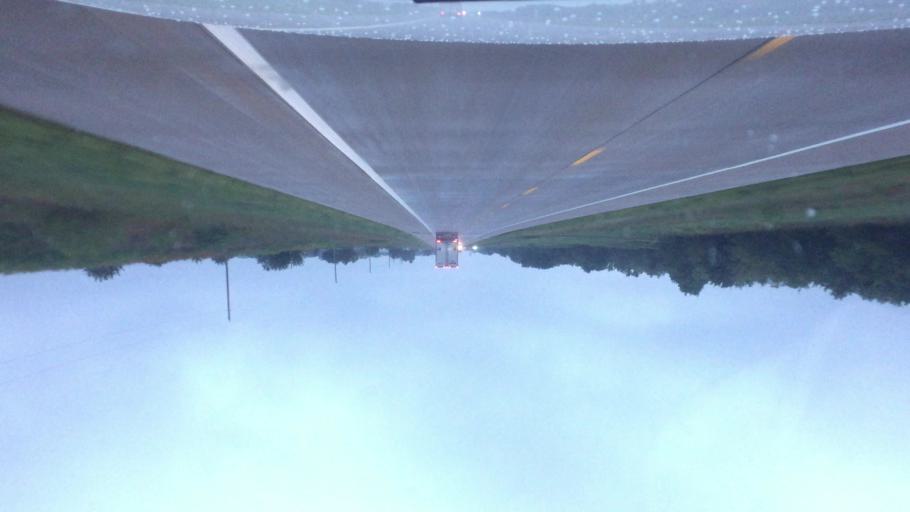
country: US
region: Kansas
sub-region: Neosho County
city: Chanute
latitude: 37.5089
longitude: -95.4709
